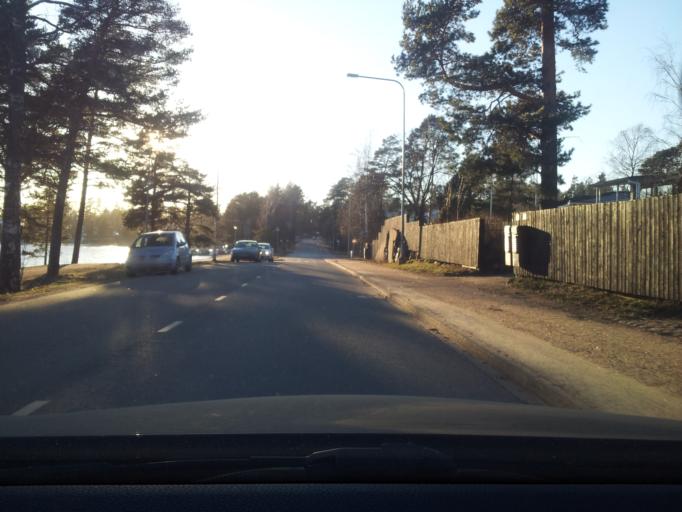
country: FI
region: Uusimaa
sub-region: Helsinki
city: Koukkuniemi
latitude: 60.1585
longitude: 24.7974
